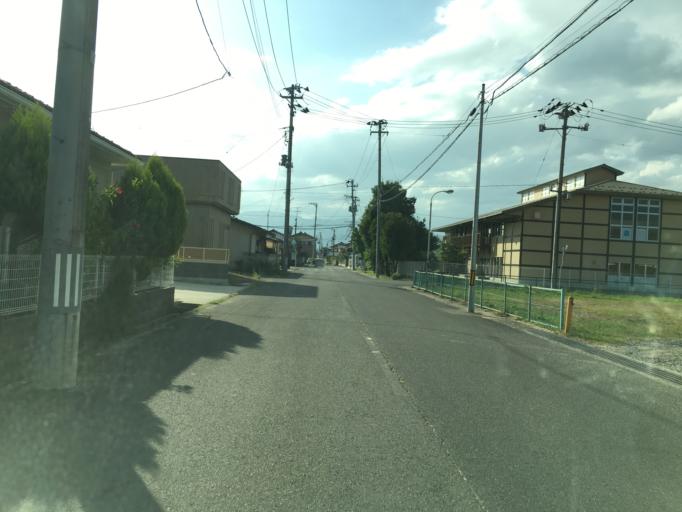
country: JP
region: Fukushima
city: Yanagawamachi-saiwaicho
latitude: 37.8537
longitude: 140.6040
